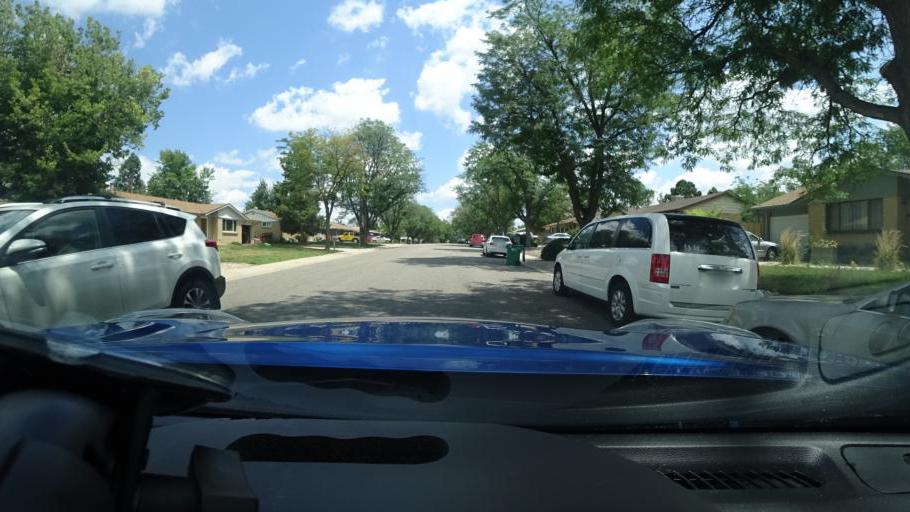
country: US
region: Colorado
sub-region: Adams County
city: Aurora
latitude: 39.7019
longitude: -104.8462
